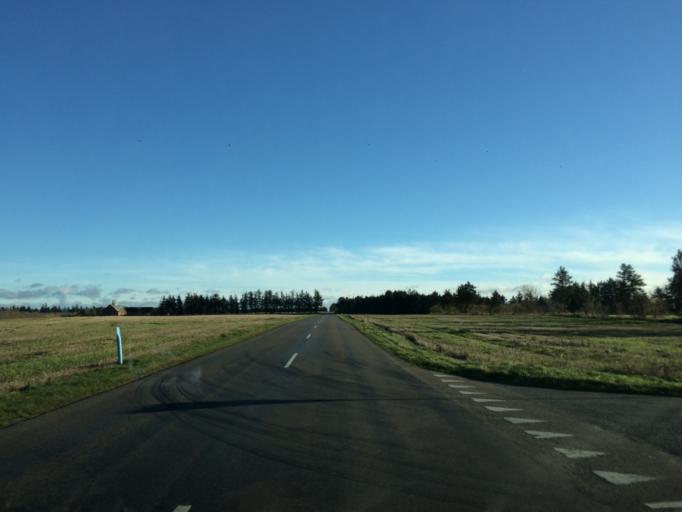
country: DK
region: Central Jutland
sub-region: Ringkobing-Skjern Kommune
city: Videbaek
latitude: 56.0831
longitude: 8.7116
